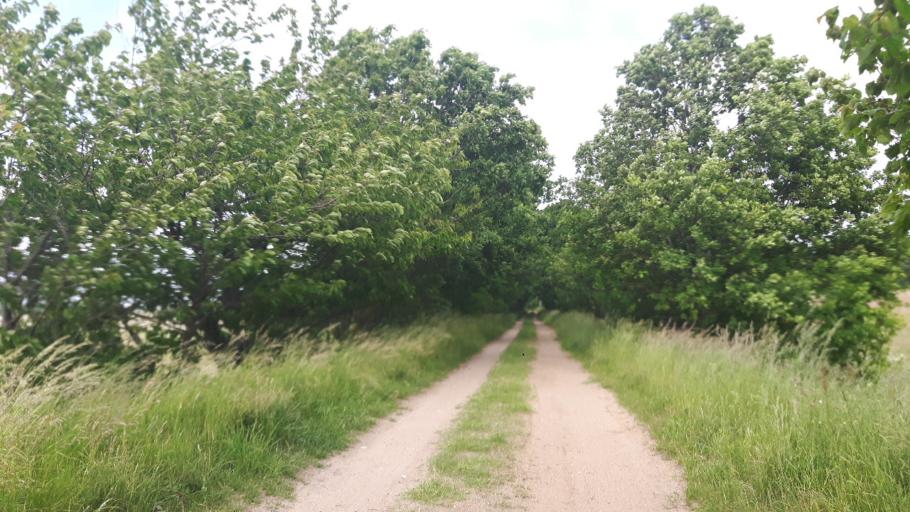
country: PL
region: Pomeranian Voivodeship
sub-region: Powiat slupski
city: Ustka
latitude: 54.5952
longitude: 16.9872
